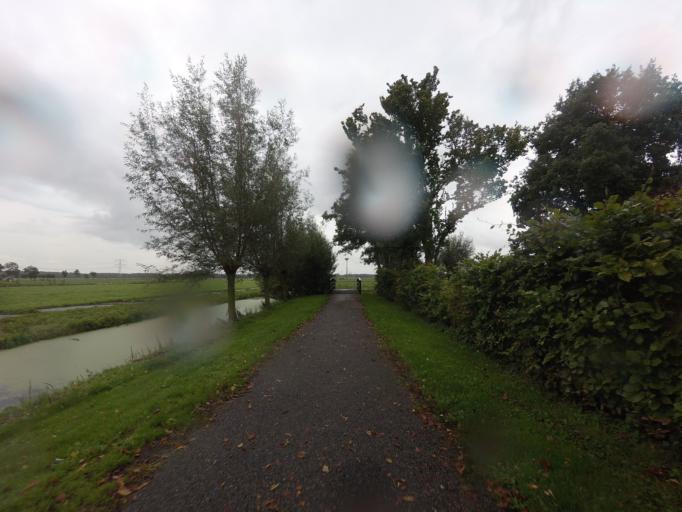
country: NL
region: South Holland
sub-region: Gemeente Papendrecht
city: Papendrecht
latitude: 51.8569
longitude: 4.7101
